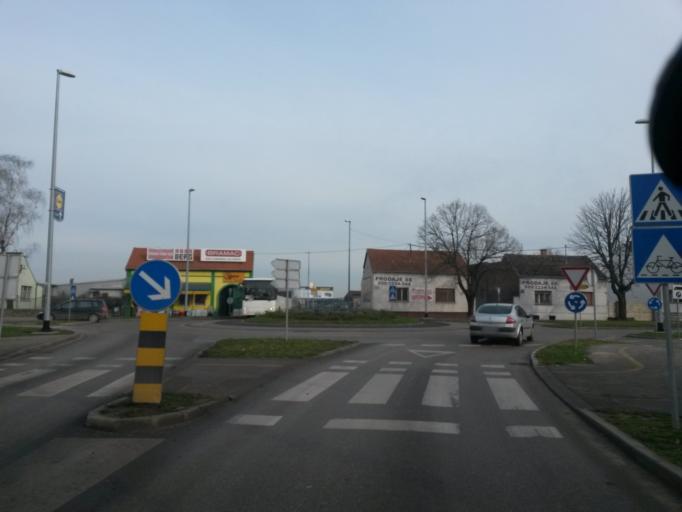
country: HR
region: Vukovarsko-Srijemska
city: Vinkovci
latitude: 45.2864
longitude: 18.8165
